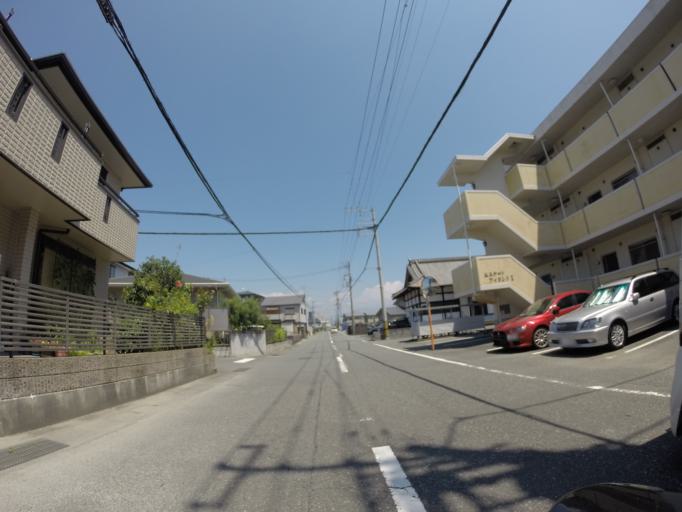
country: JP
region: Shizuoka
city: Fuji
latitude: 35.1455
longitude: 138.6434
